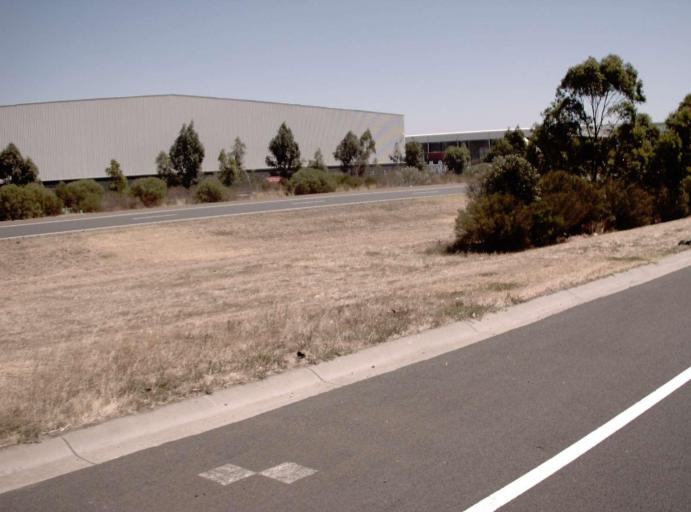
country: AU
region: Victoria
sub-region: Brimbank
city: Derrimut
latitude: -37.7937
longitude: 144.7872
